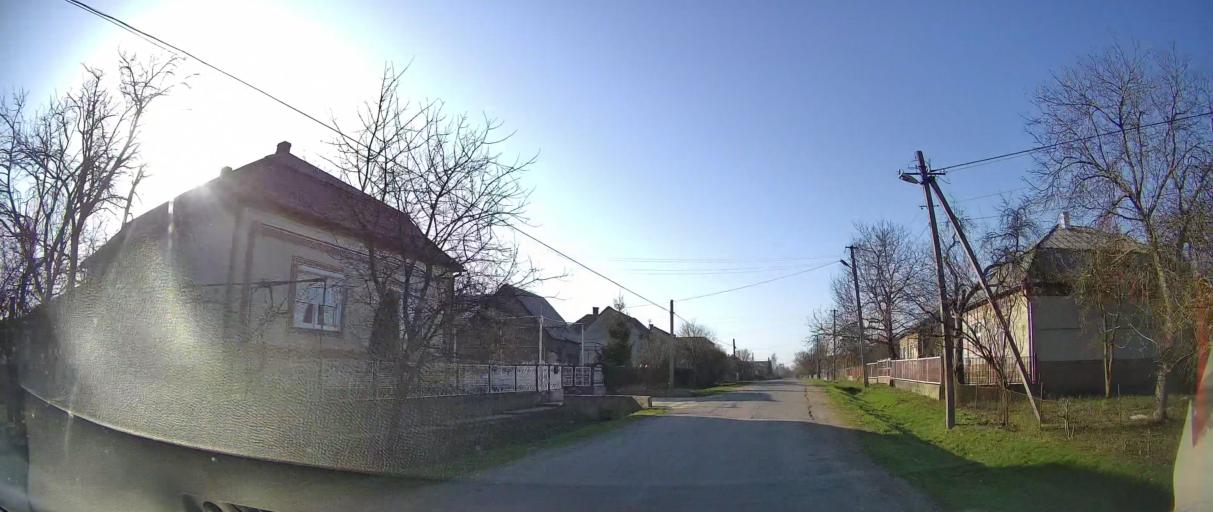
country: UA
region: Zakarpattia
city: Storozhnytsya
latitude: 48.5684
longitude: 22.1736
